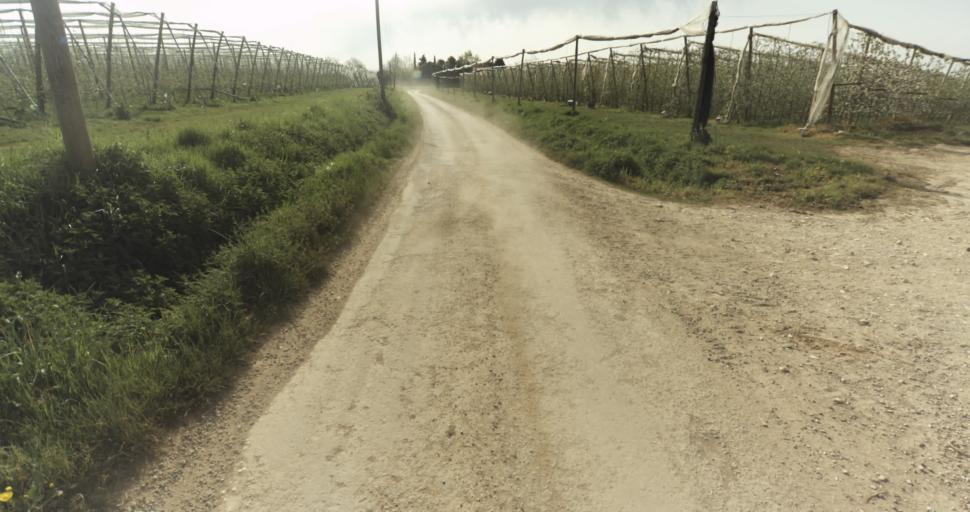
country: FR
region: Midi-Pyrenees
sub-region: Departement du Tarn-et-Garonne
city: Moissac
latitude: 44.1015
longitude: 1.1209
